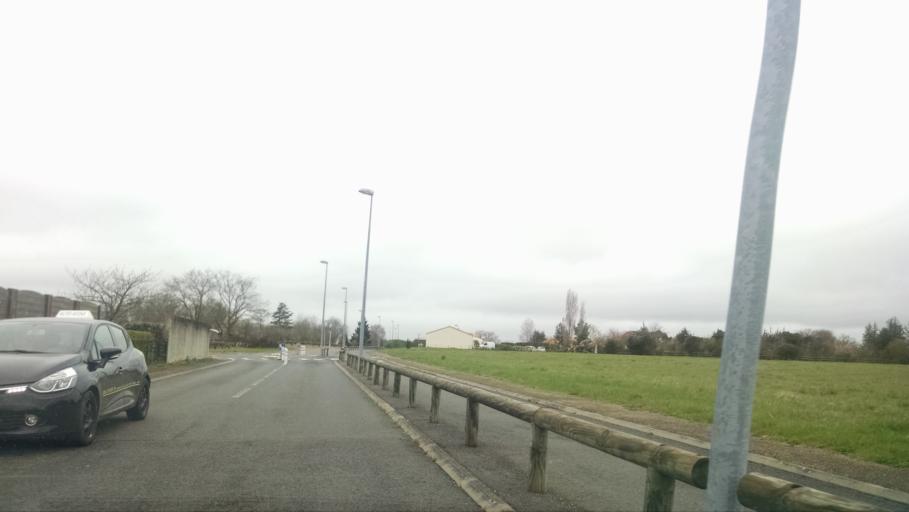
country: FR
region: Pays de la Loire
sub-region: Departement de la Loire-Atlantique
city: Vallet
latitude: 47.1725
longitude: -1.2673
